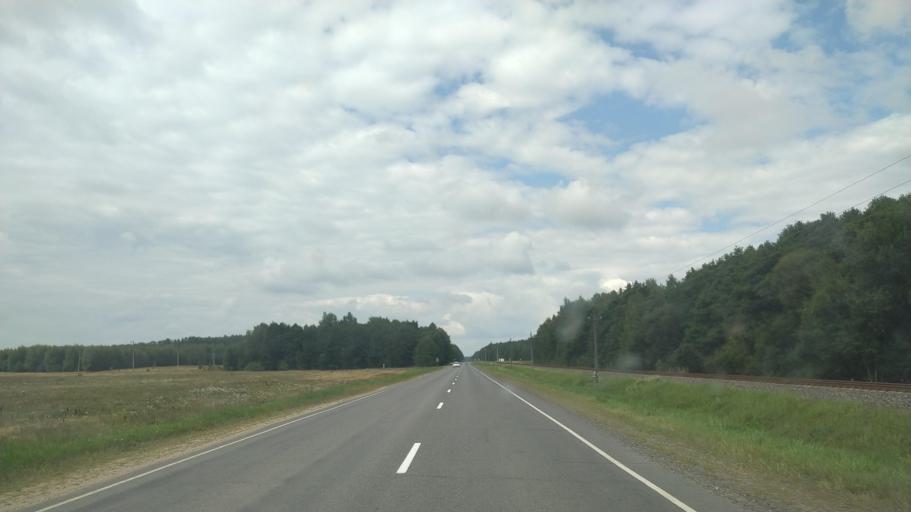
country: BY
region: Brest
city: Byelaazyorsk
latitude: 52.5381
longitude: 25.1395
